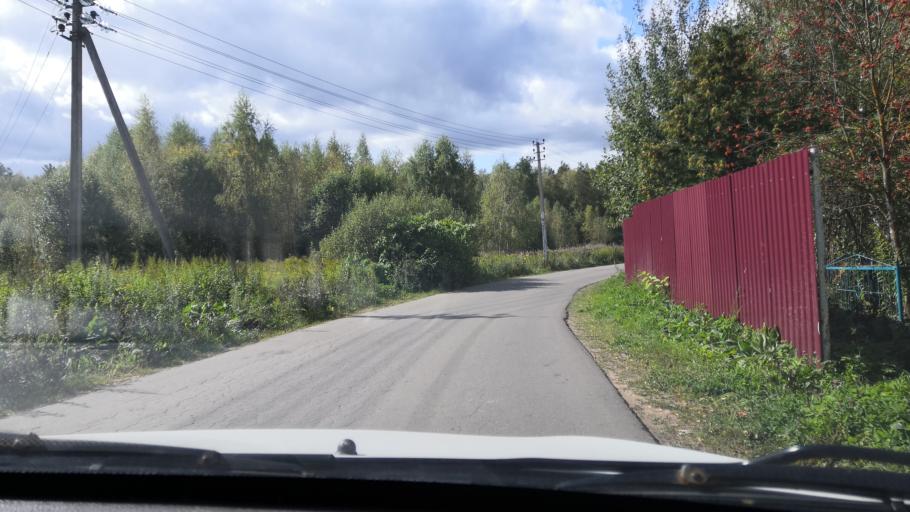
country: RU
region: Moskovskaya
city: Povarovo
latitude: 56.0646
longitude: 37.0412
